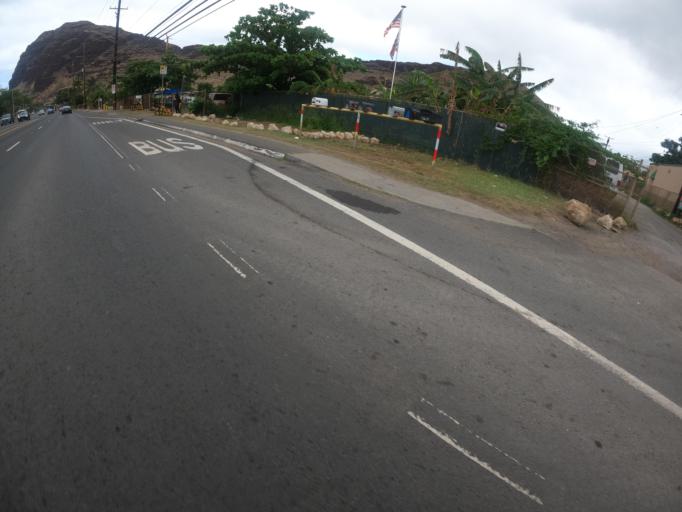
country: US
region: Hawaii
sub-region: Honolulu County
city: Nanakuli
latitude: 21.3949
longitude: -158.1601
